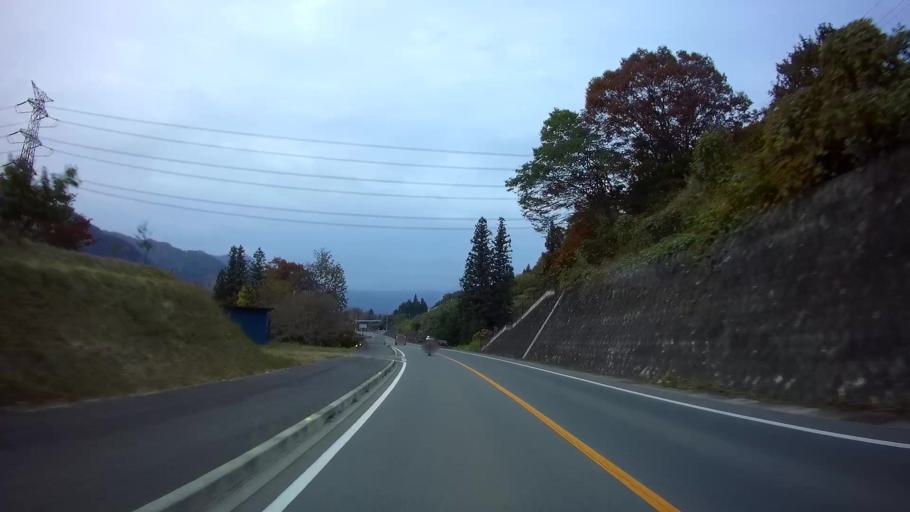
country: JP
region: Gunma
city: Nakanojomachi
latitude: 36.5612
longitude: 138.7532
